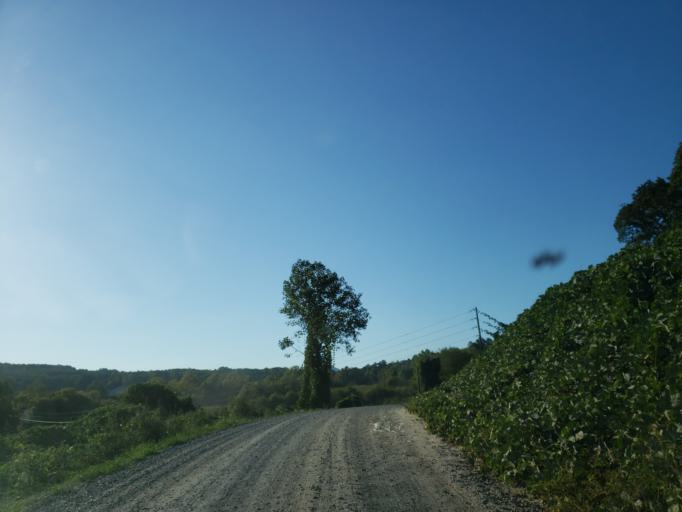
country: US
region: Georgia
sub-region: Pickens County
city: Nelson
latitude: 34.4016
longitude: -84.4260
